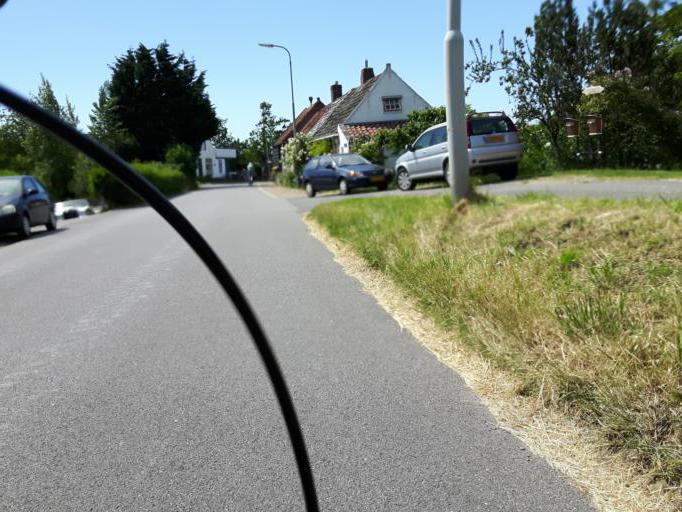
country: NL
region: Zeeland
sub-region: Gemeente Goes
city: Goes
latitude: 51.5263
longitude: 3.8254
